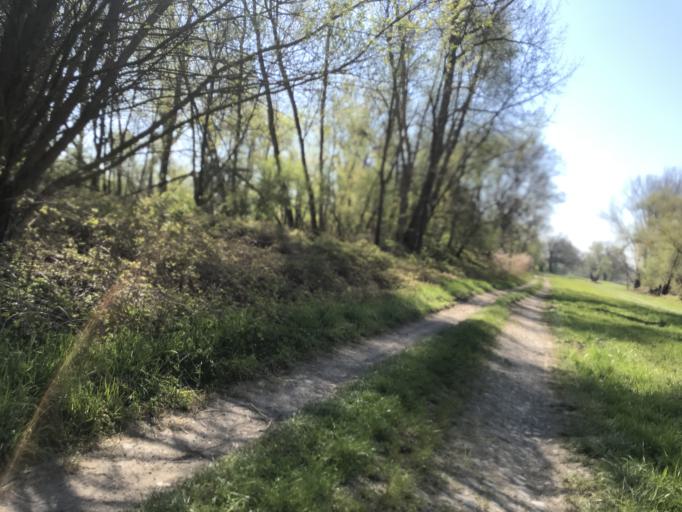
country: DE
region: Hesse
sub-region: Regierungsbezirk Darmstadt
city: Ginsheim-Gustavsburg
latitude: 49.9508
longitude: 8.3508
